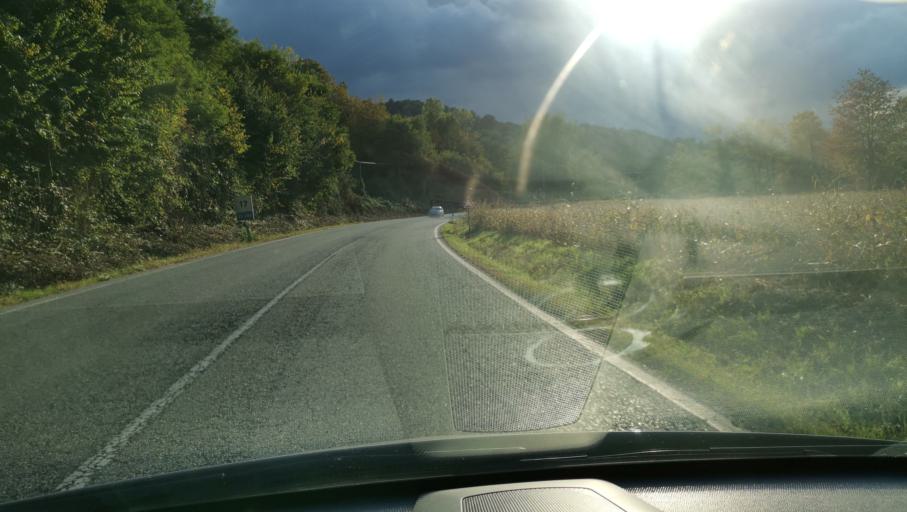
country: IT
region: Piedmont
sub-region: Provincia di Torino
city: Castagneto Po
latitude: 45.1728
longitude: 7.8775
